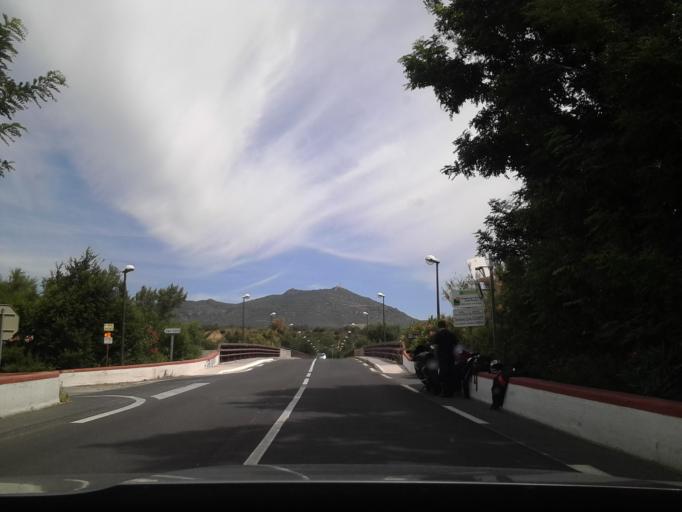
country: FR
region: Languedoc-Roussillon
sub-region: Departement des Pyrenees-Orientales
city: Millas
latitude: 42.6950
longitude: 2.6968
